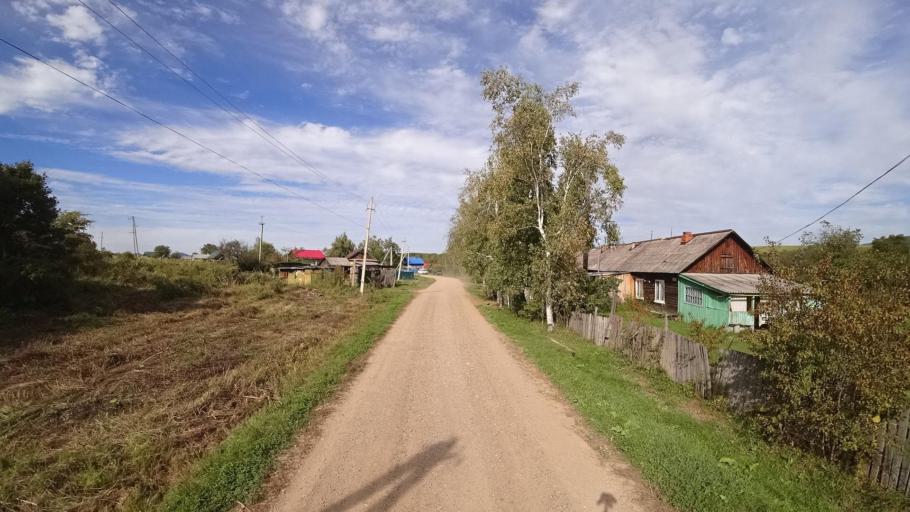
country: RU
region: Primorskiy
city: Dostoyevka
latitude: 44.2980
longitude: 133.4635
